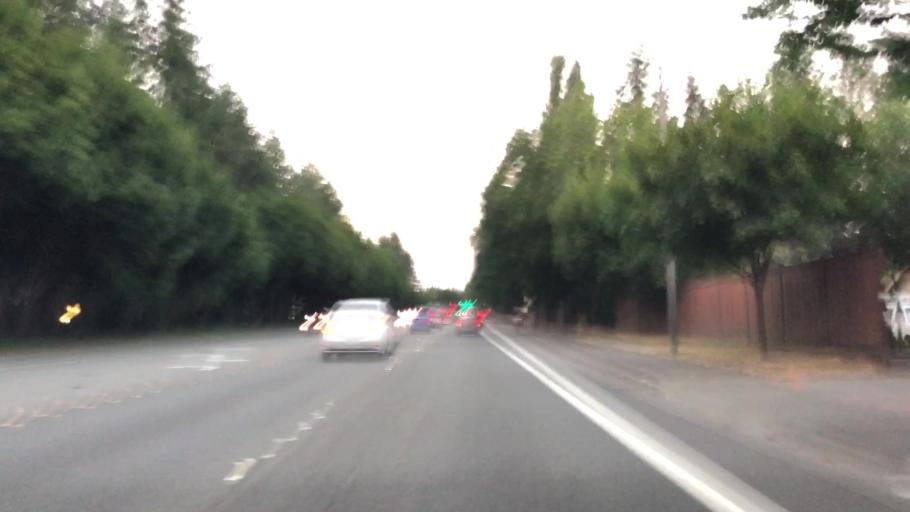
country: US
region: Washington
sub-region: King County
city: Redmond
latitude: 47.6828
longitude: -122.0993
